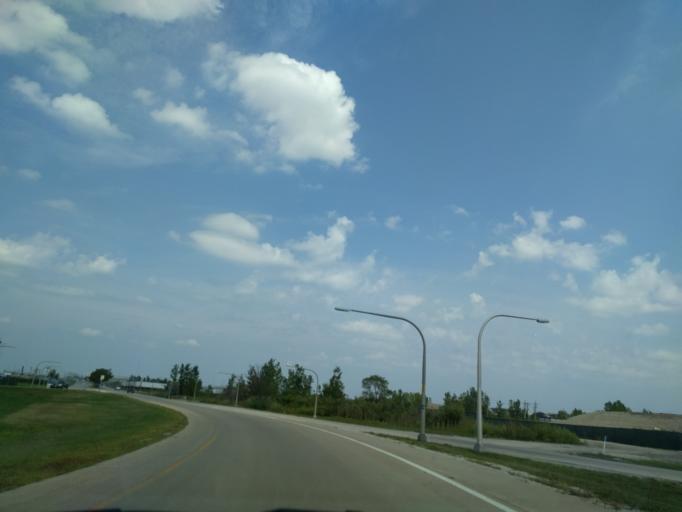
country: US
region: Illinois
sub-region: Cook County
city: Schiller Park
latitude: 41.9713
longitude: -87.8760
